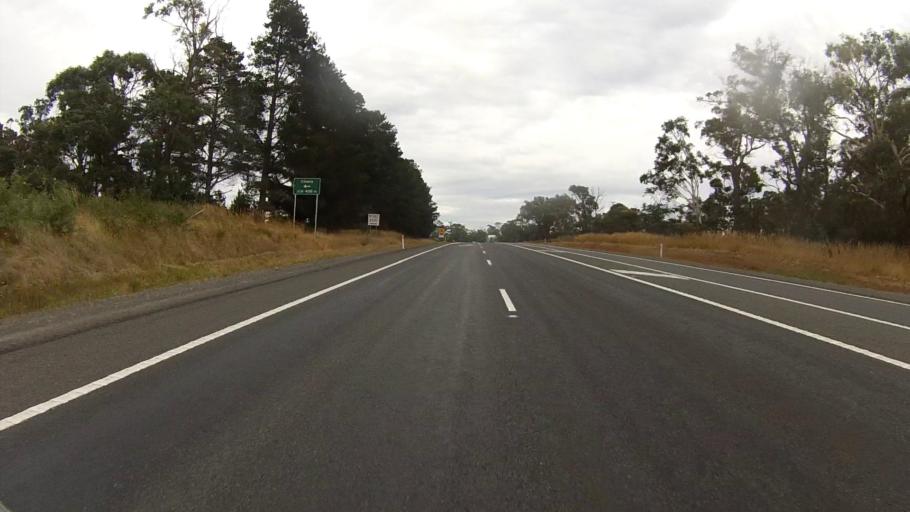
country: AU
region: Tasmania
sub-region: Northern Midlands
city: Evandale
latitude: -41.8321
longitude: 147.4439
